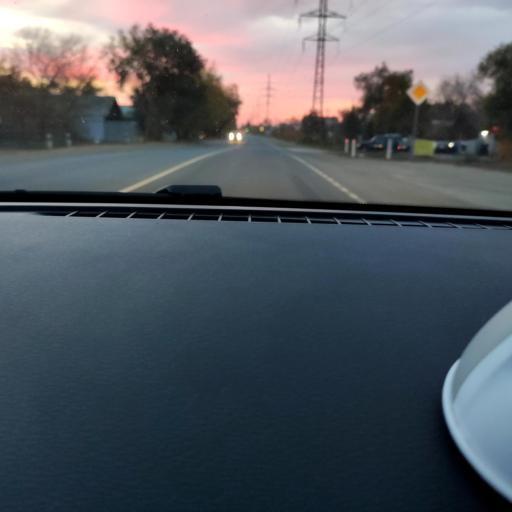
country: RU
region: Samara
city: Samara
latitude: 53.1323
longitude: 50.1360
